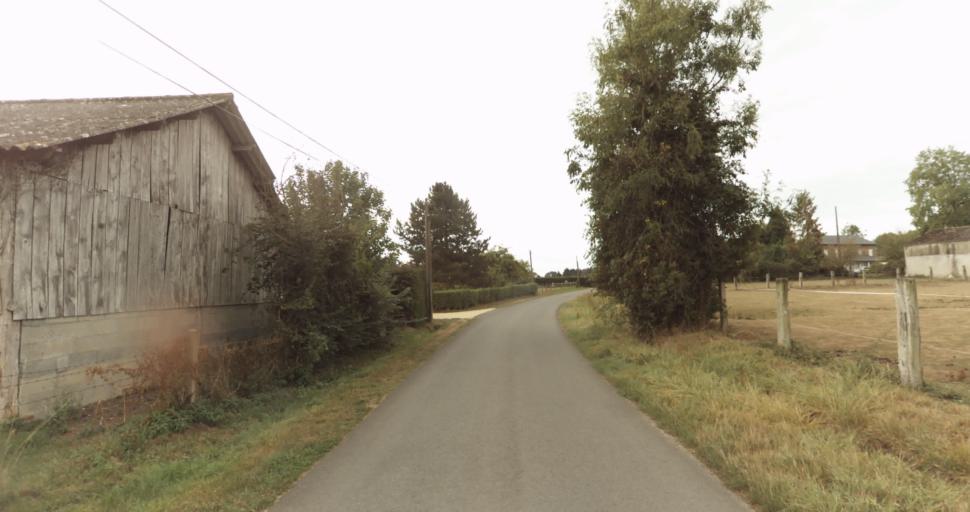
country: FR
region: Lower Normandy
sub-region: Departement de l'Orne
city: Vimoutiers
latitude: 48.9495
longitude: 0.2512
